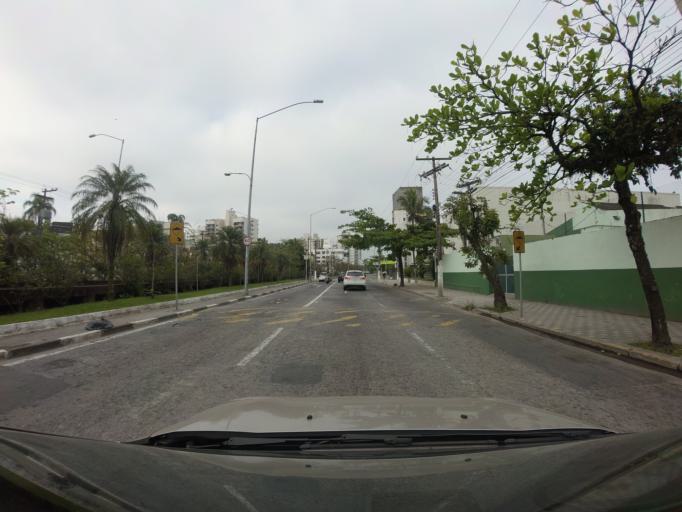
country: BR
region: Sao Paulo
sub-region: Guaruja
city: Guaruja
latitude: -23.9887
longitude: -46.2476
